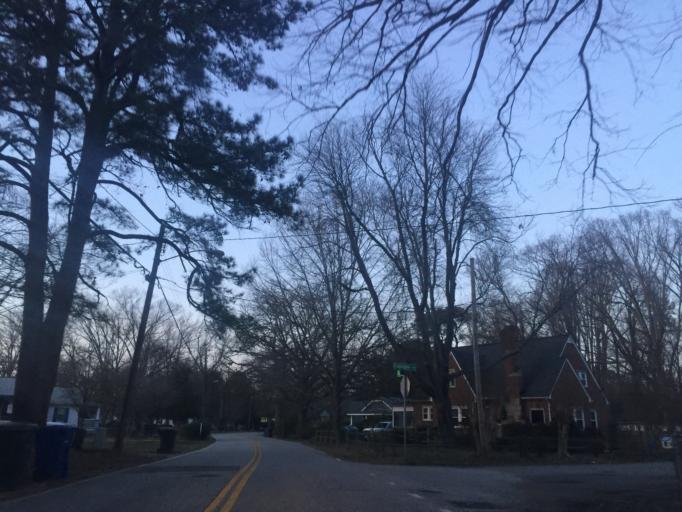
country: US
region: Virginia
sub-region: City of Newport News
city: Newport News
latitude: 37.0791
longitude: -76.5012
